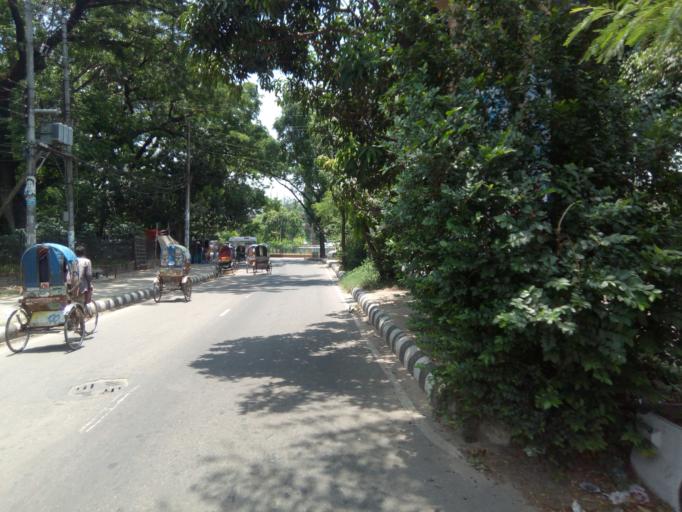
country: BD
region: Dhaka
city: Azimpur
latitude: 23.7286
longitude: 90.3997
